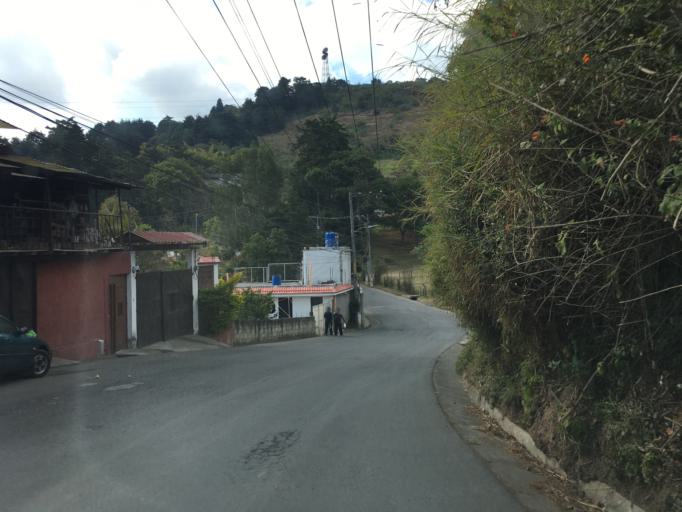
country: GT
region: Guatemala
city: San Jose Pinula
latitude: 14.5595
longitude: -90.4404
